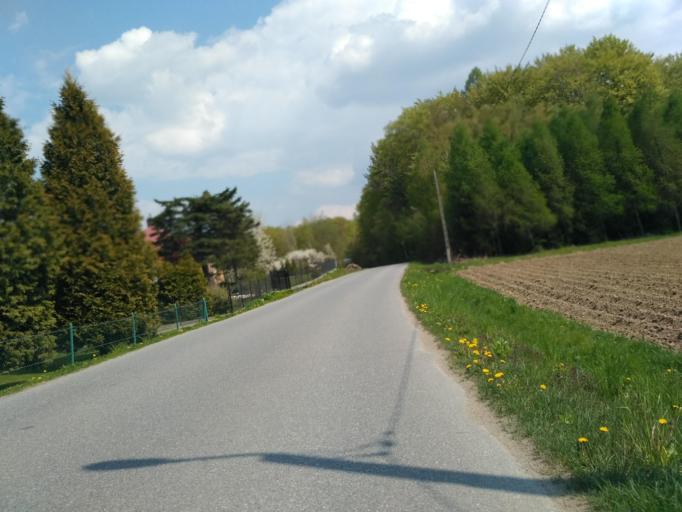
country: PL
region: Subcarpathian Voivodeship
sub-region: Powiat jasielski
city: Debowiec
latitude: 49.6988
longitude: 21.5081
